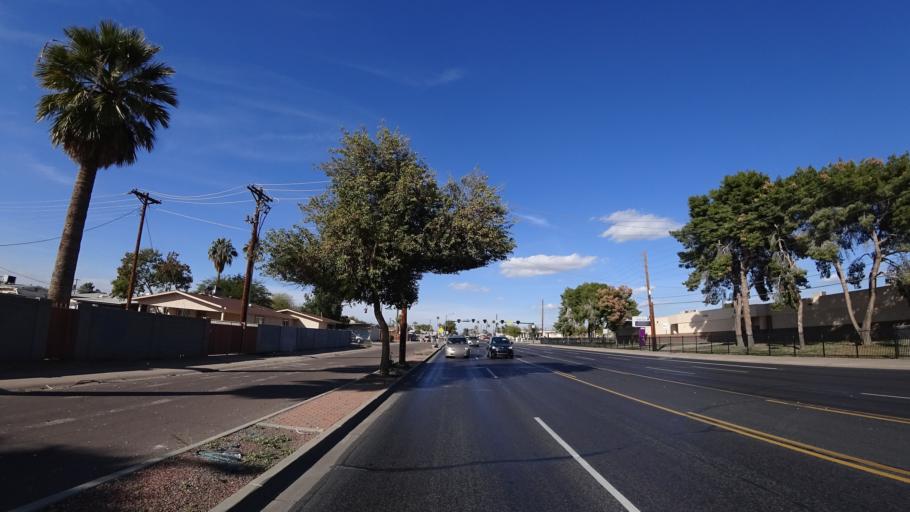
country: US
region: Arizona
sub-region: Maricopa County
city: Tolleson
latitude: 33.4903
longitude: -112.2207
